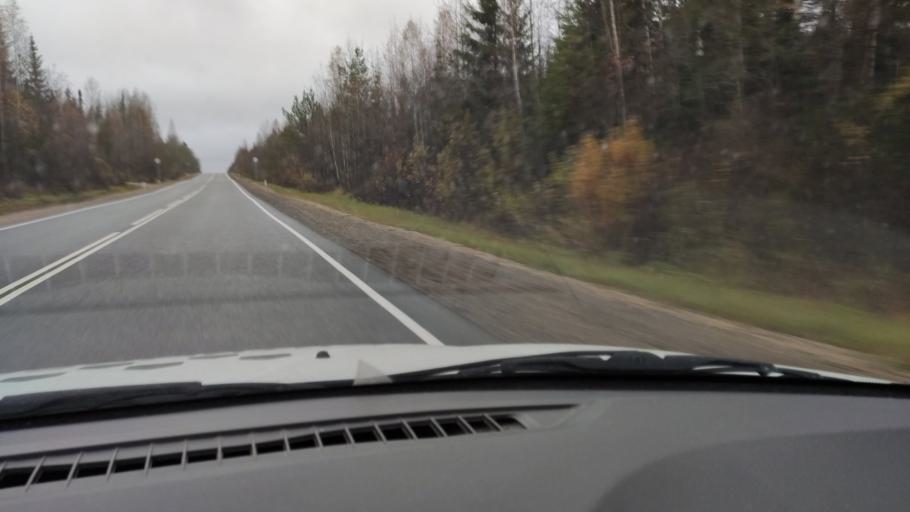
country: RU
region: Kirov
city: Omutninsk
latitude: 58.7152
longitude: 52.0926
